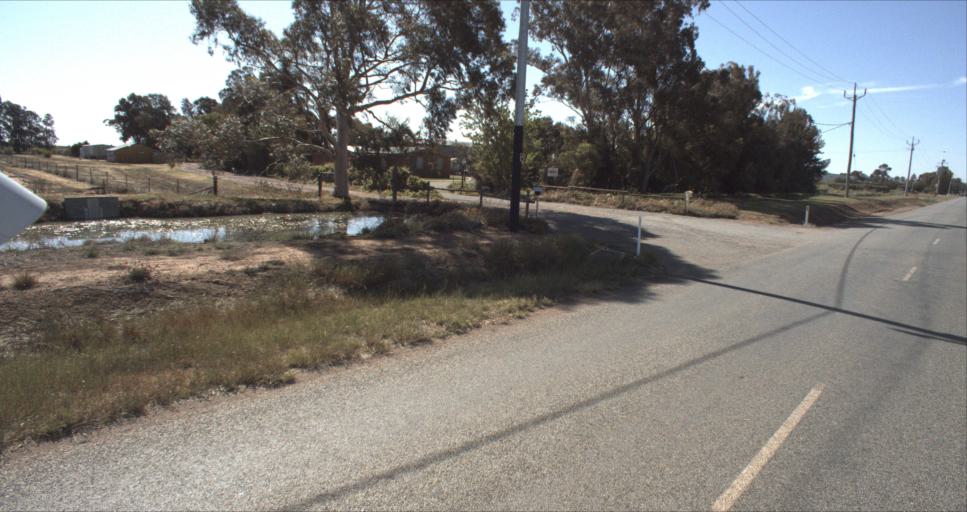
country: AU
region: New South Wales
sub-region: Leeton
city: Leeton
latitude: -34.5630
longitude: 146.3832
